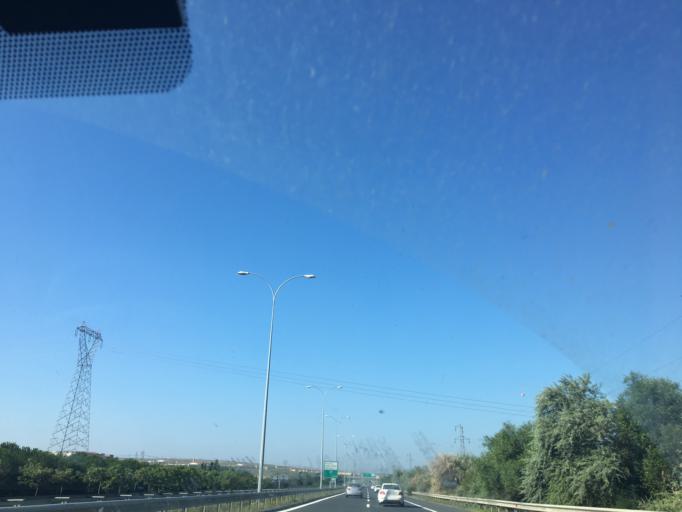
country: TR
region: Istanbul
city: Canta
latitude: 41.1037
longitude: 28.1564
